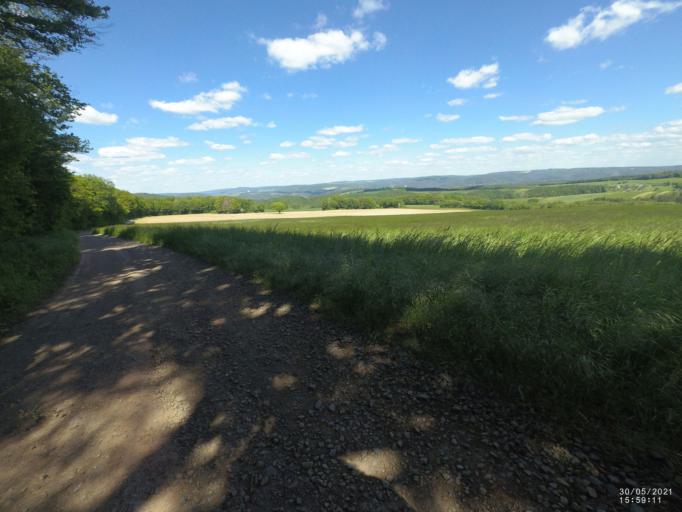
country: DE
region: Rheinland-Pfalz
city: Waldesch
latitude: 50.2673
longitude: 7.5551
